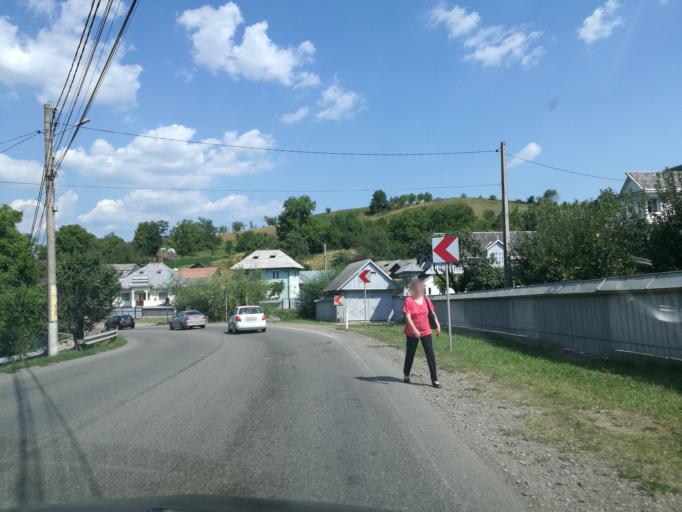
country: RO
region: Neamt
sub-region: Comuna Baltatesti
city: Baltatesti
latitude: 47.1177
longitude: 26.3127
